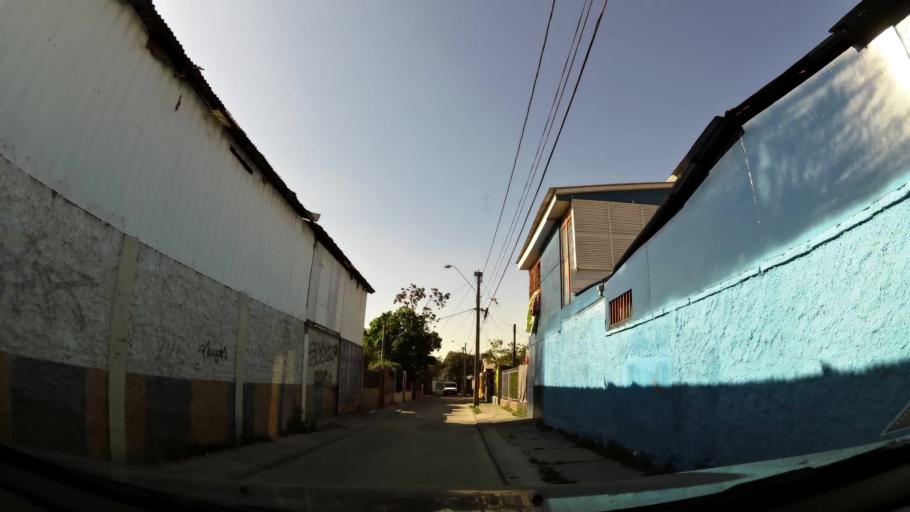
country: CL
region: Santiago Metropolitan
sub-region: Provincia de Santiago
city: La Pintana
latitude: -33.5763
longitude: -70.6531
